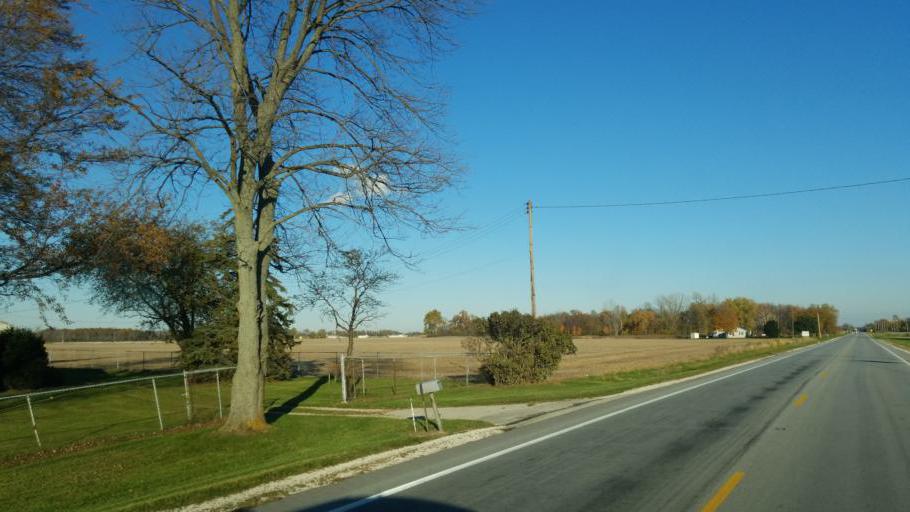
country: US
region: Ohio
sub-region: Sandusky County
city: Stony Prairie
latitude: 41.3417
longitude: -83.2136
